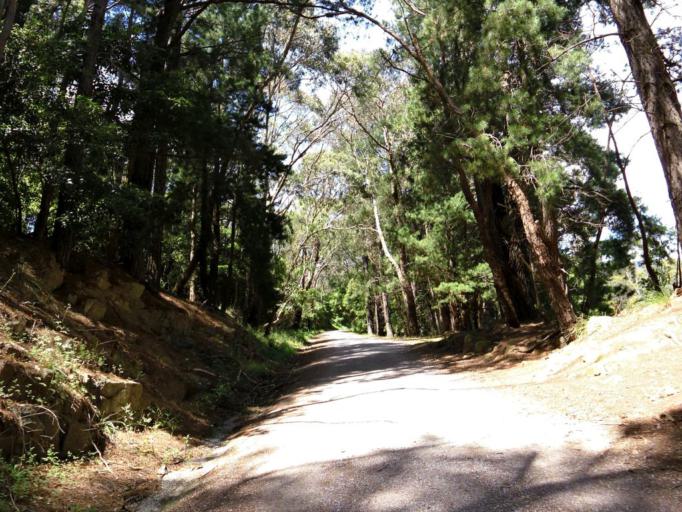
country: AU
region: Victoria
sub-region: Yarra Ranges
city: Mount Evelyn
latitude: -37.7775
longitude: 145.3780
